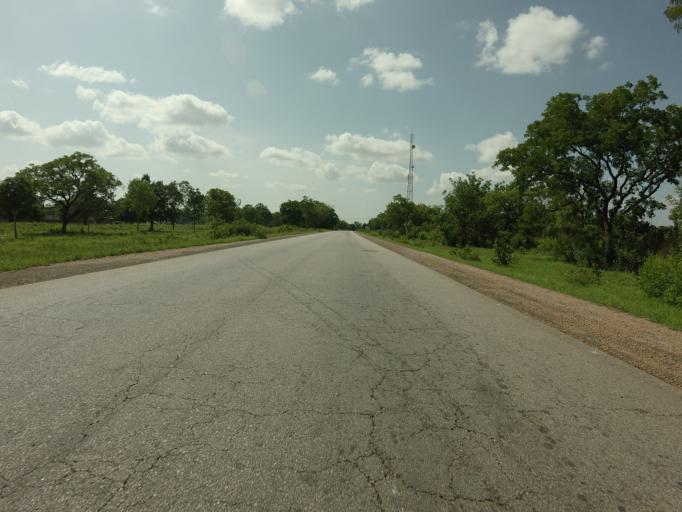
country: GH
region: Northern
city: Savelugu
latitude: 9.8159
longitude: -0.8622
